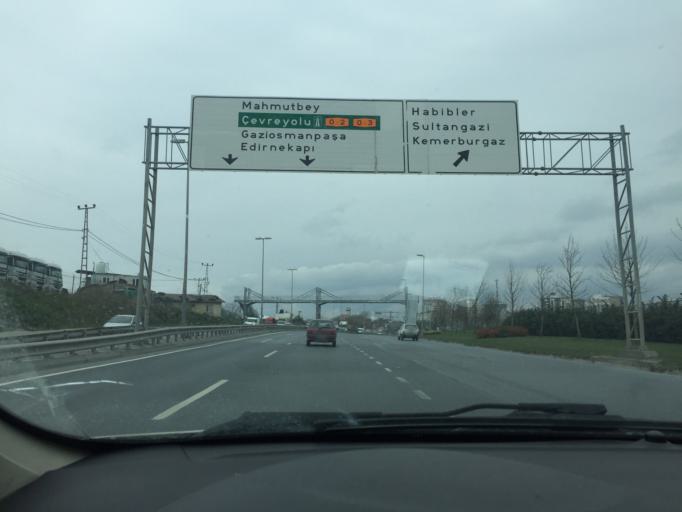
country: TR
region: Istanbul
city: Basaksehir
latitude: 41.1362
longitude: 28.8187
